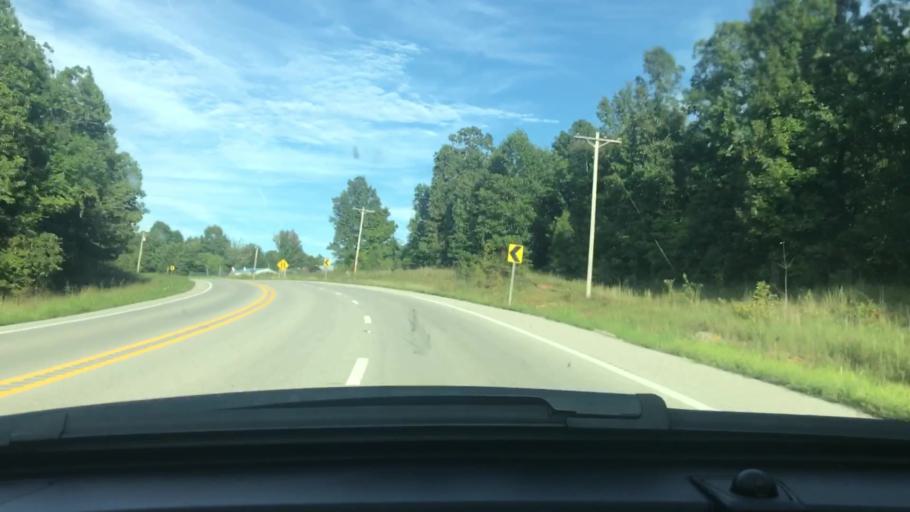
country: US
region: Arkansas
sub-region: Sharp County
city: Cherokee Village
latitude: 36.2738
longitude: -91.3196
